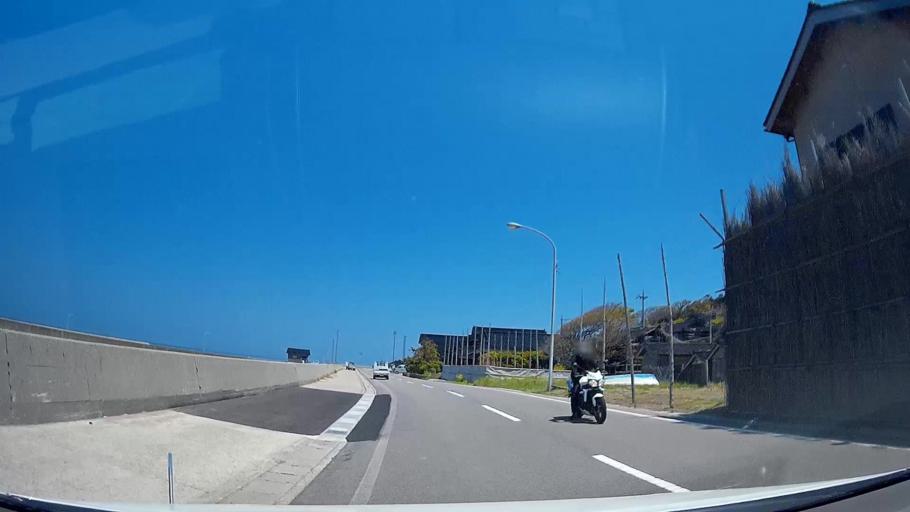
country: JP
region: Ishikawa
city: Nanao
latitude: 37.5279
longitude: 137.2868
